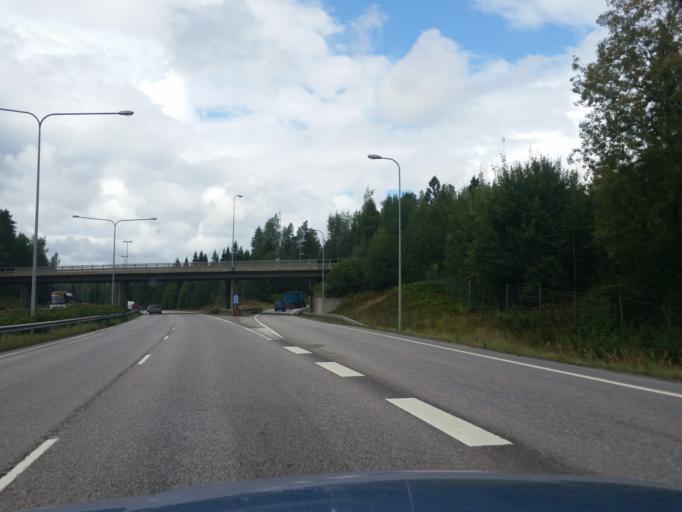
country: FI
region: Uusimaa
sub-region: Helsinki
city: Espoo
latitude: 60.2435
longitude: 24.5692
